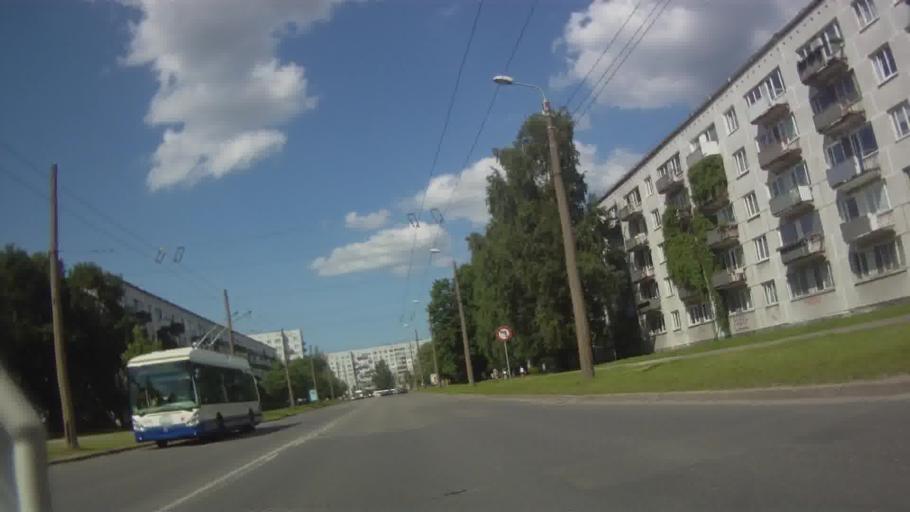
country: LV
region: Riga
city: Riga
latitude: 56.9560
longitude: 24.1760
